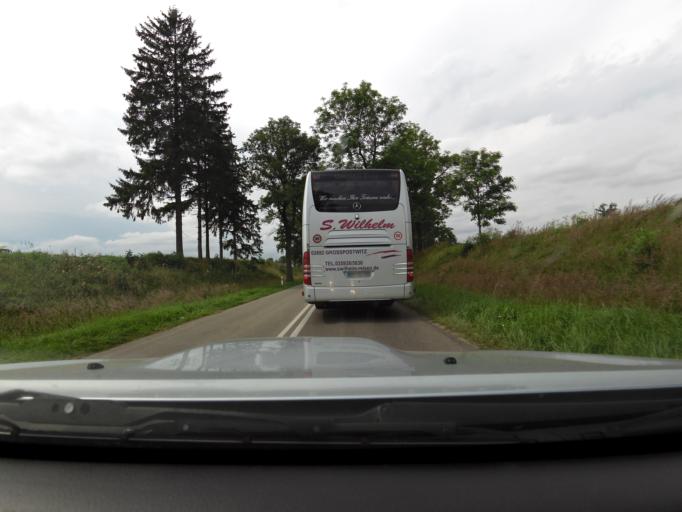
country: PL
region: Warmian-Masurian Voivodeship
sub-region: Powiat ketrzynski
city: Ketrzyn
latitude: 54.0720
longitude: 21.3137
